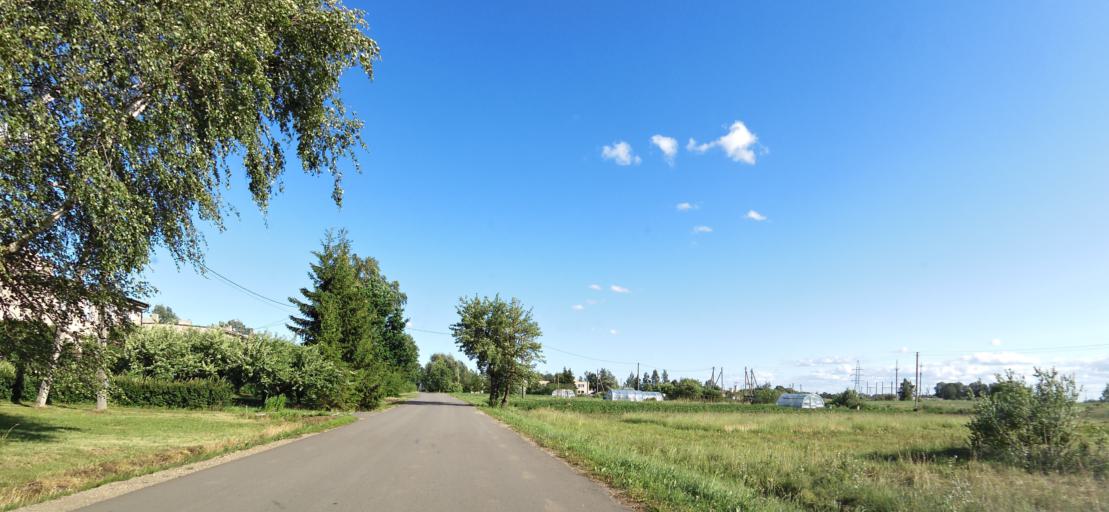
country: LT
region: Panevezys
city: Pasvalys
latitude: 56.1348
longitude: 24.5379
